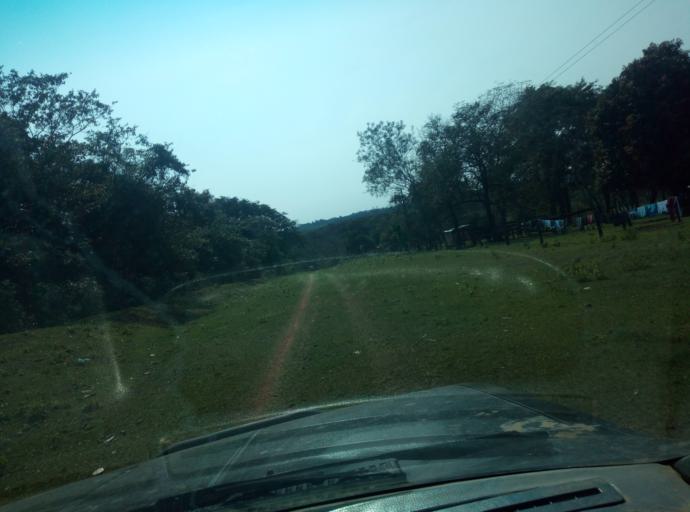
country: PY
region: Caaguazu
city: Carayao
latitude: -25.3029
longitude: -56.3234
